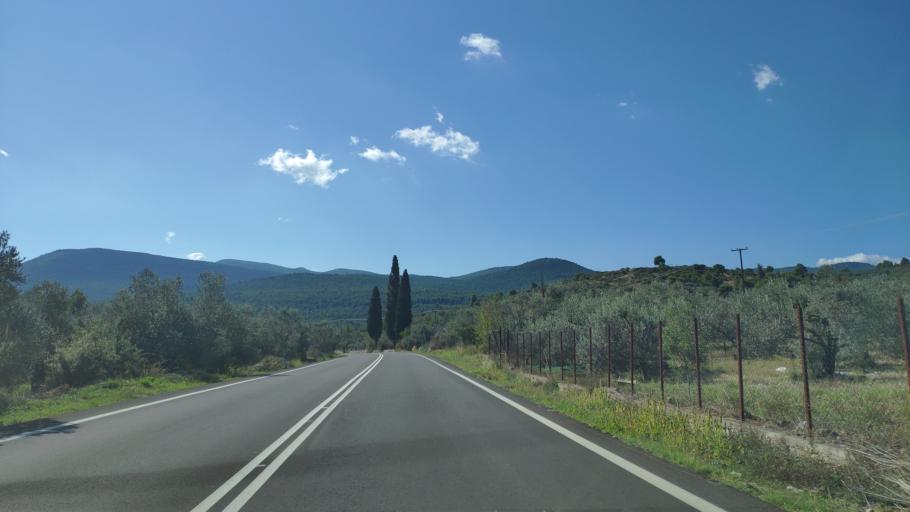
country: GR
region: Peloponnese
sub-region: Nomos Korinthias
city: Sofikon
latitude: 37.8012
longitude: 23.0780
